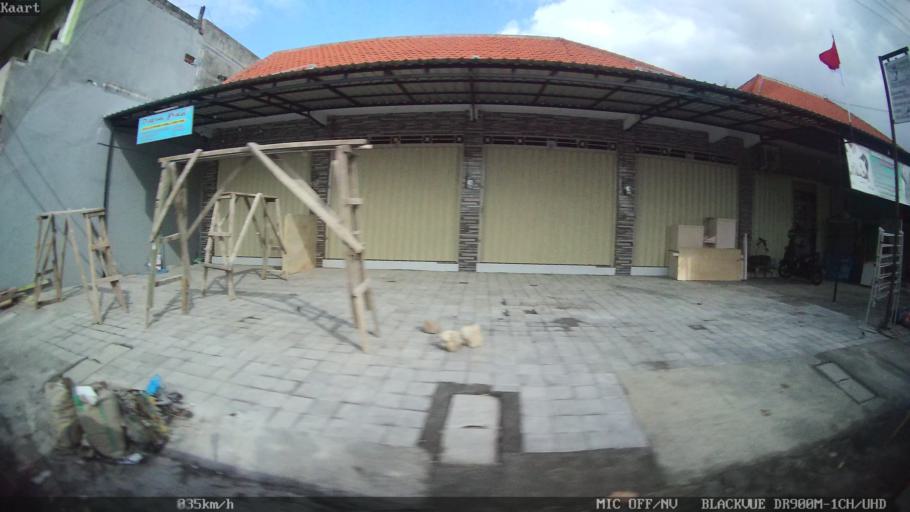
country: ID
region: Bali
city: Karyadharma
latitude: -8.7005
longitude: 115.1941
